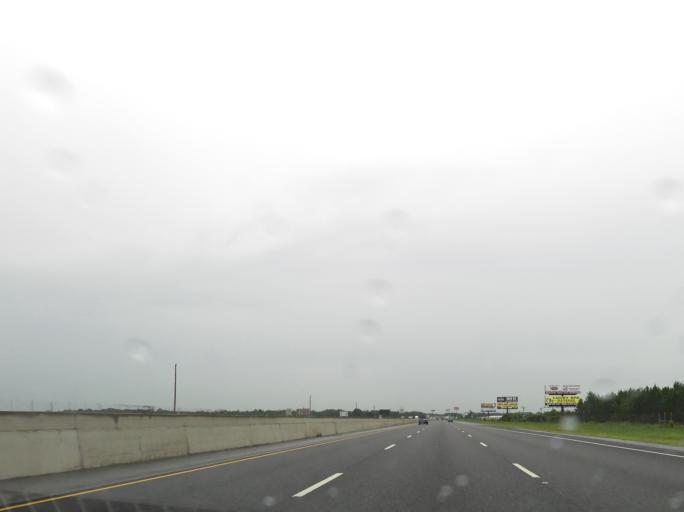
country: US
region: Georgia
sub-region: Turner County
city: Ashburn
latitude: 31.7050
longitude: -83.6343
